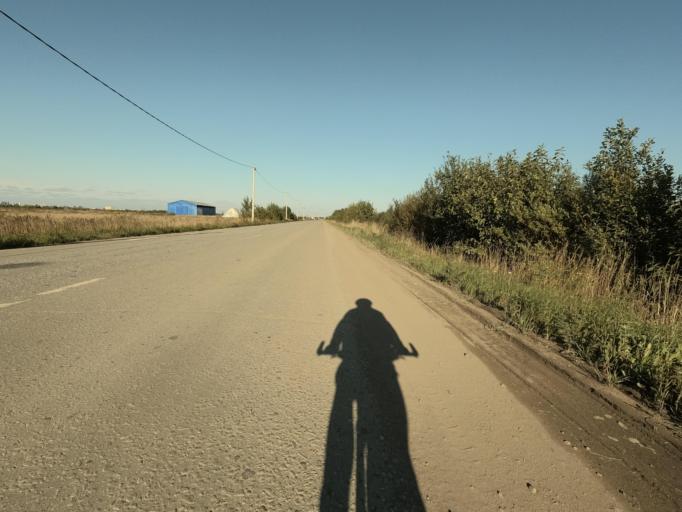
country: RU
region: St.-Petersburg
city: Petro-Slavyanka
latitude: 59.7655
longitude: 30.4869
